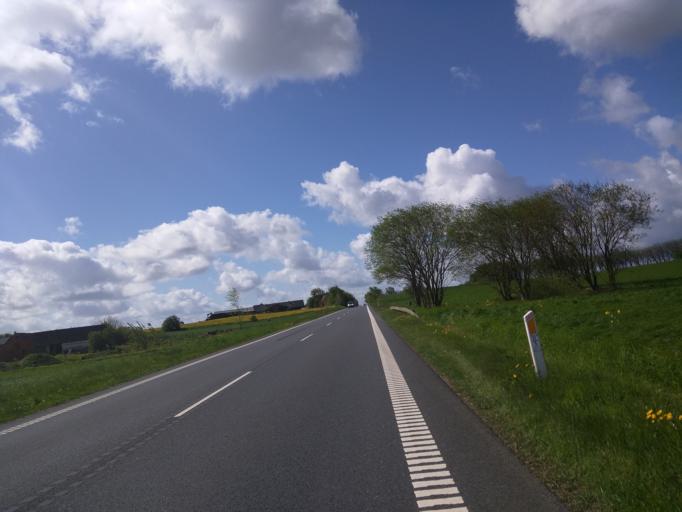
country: DK
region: Central Jutland
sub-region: Silkeborg Kommune
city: Kjellerup
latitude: 56.3591
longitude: 9.4365
